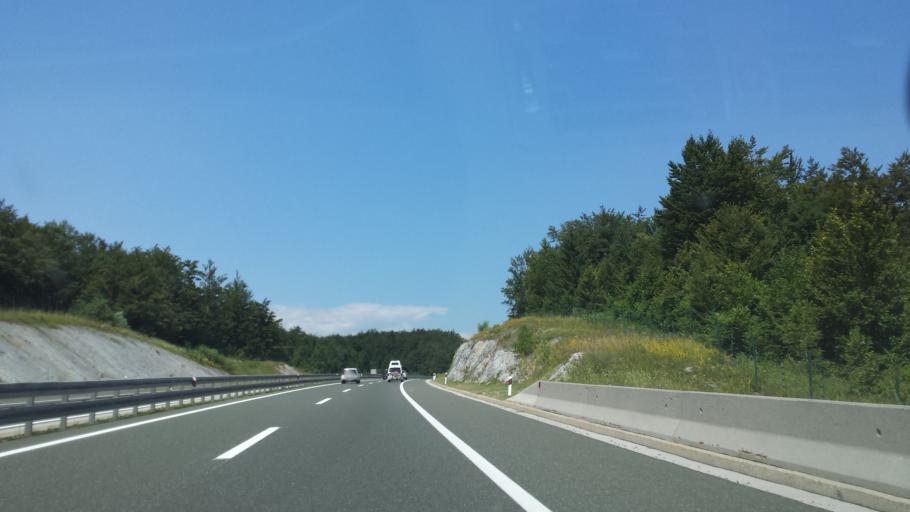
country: HR
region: Primorsko-Goranska
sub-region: Grad Delnice
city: Delnice
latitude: 45.3843
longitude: 14.8391
